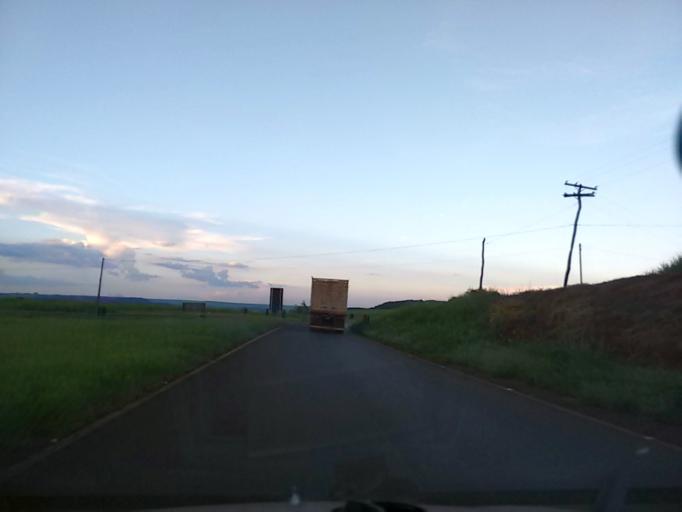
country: BR
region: Sao Paulo
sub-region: Boa Esperanca Do Sul
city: Boa Esperanca do Sul
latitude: -22.1201
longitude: -48.4563
